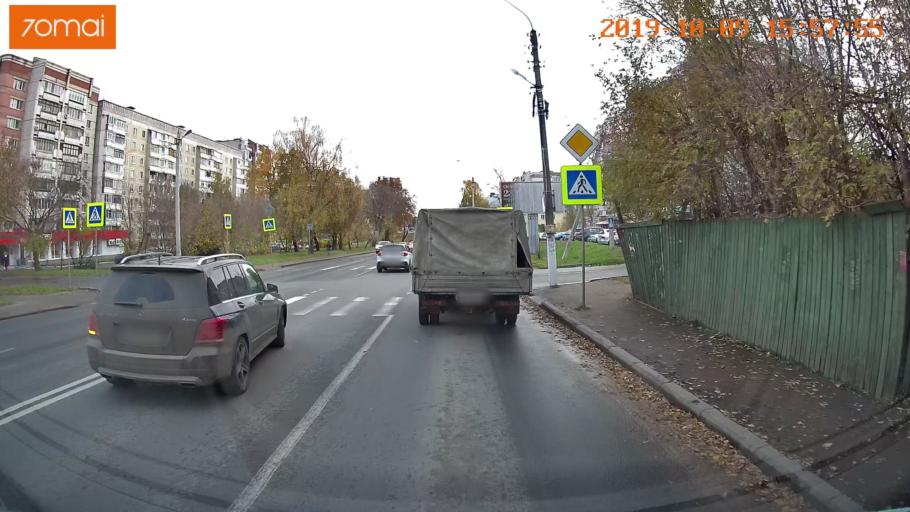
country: RU
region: Kostroma
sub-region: Kostromskoy Rayon
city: Kostroma
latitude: 57.7688
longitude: 40.9508
